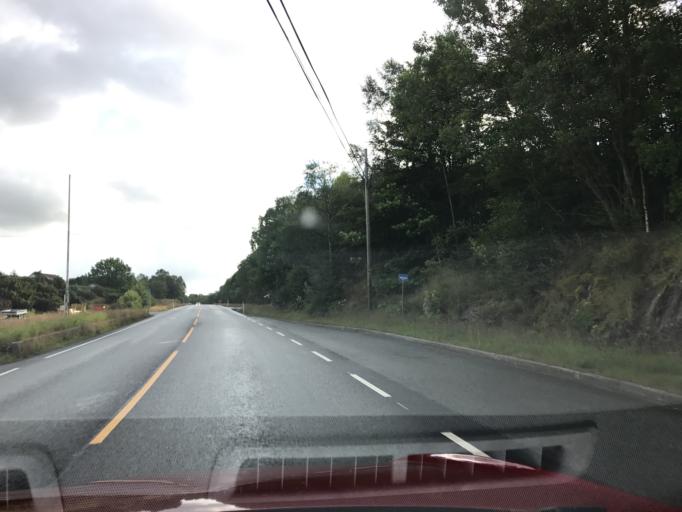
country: NO
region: Hordaland
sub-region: Sveio
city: Sveio
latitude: 59.5505
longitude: 5.3955
